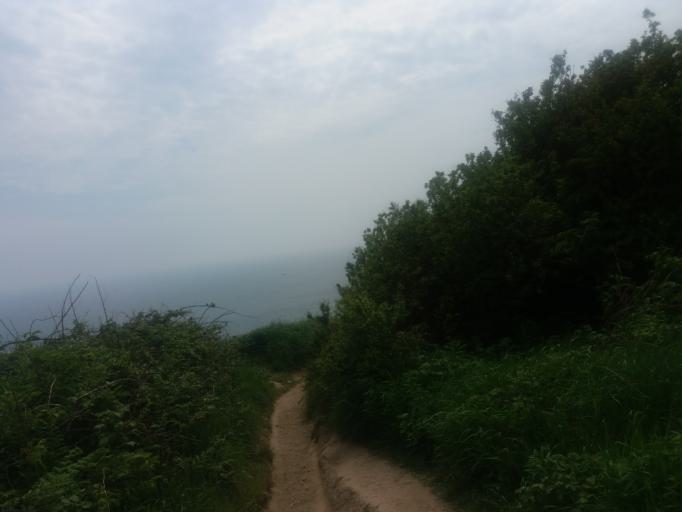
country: IE
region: Leinster
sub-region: Fingal County
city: Howth
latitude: 53.3693
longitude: -6.0539
